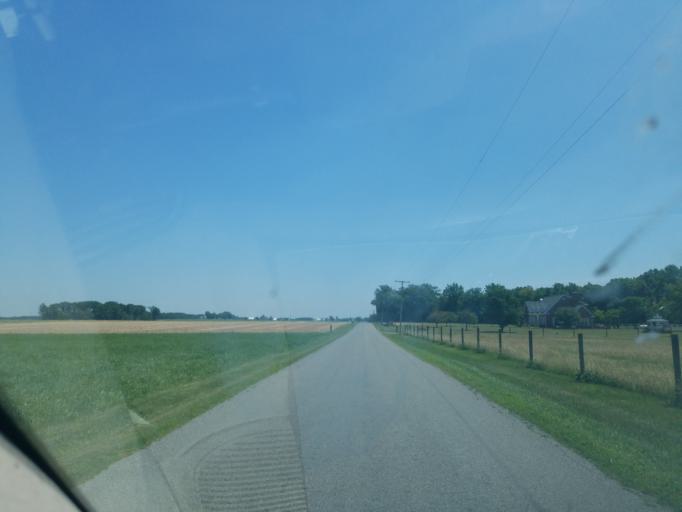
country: US
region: Ohio
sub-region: Allen County
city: Spencerville
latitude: 40.7576
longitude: -84.3935
